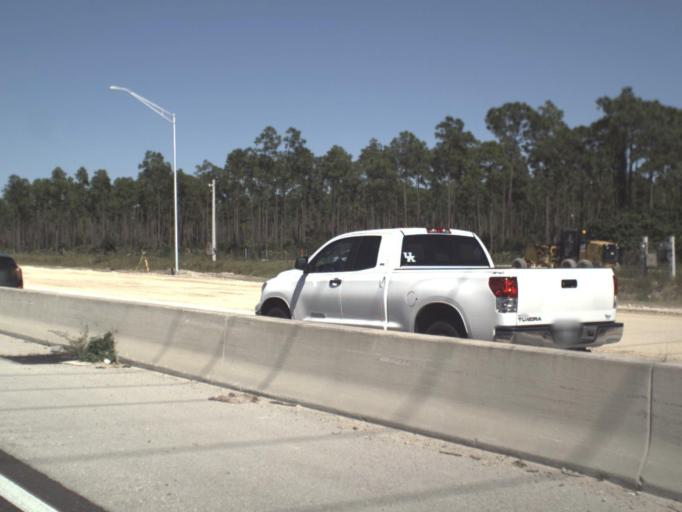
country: US
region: Florida
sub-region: Lee County
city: Three Oaks
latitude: 26.4999
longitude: -81.7943
